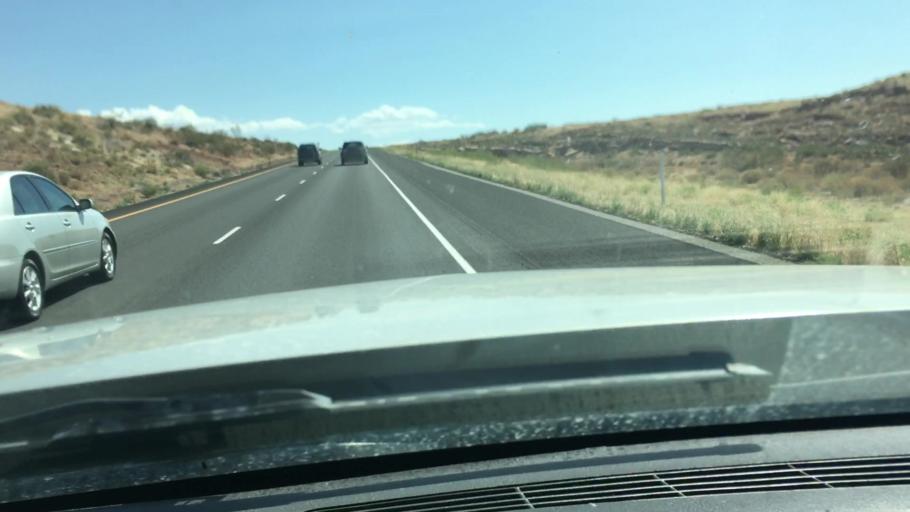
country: US
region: Utah
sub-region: Washington County
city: Washington
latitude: 37.1885
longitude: -113.4105
